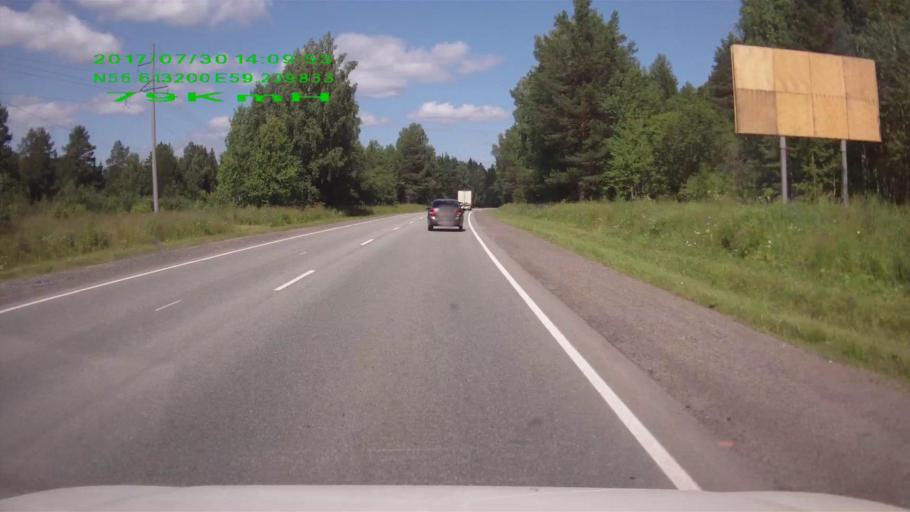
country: RU
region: Sverdlovsk
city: Nizhniye Sergi
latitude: 56.6134
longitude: 59.2299
